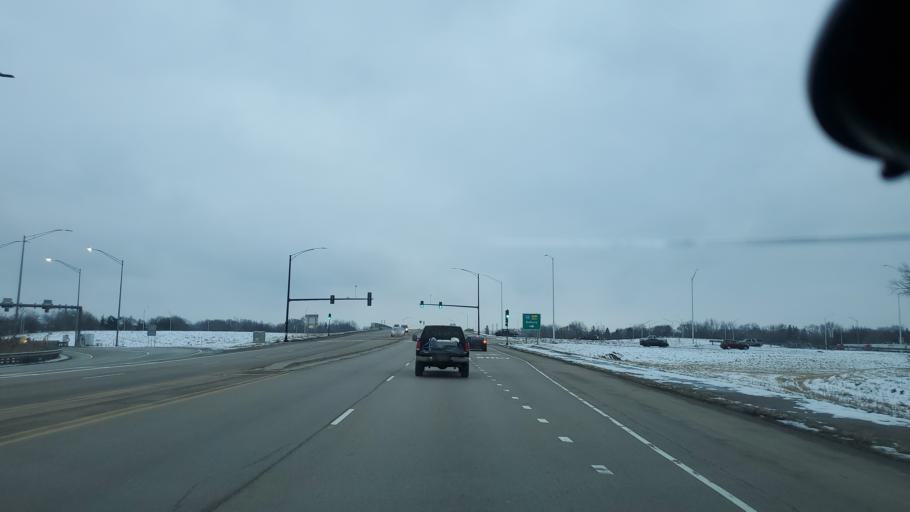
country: US
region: Illinois
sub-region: Kane County
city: North Aurora
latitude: 41.8013
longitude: -88.2822
